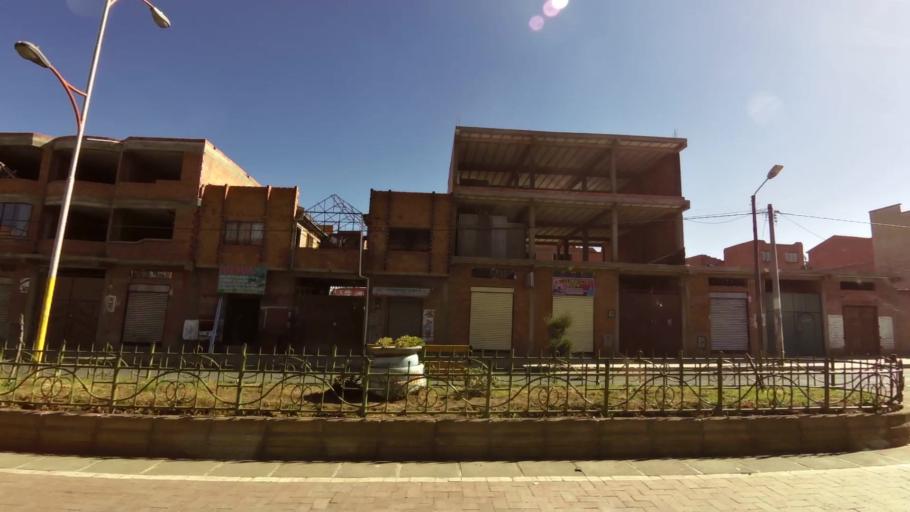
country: BO
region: La Paz
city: La Paz
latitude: -16.5236
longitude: -68.1962
